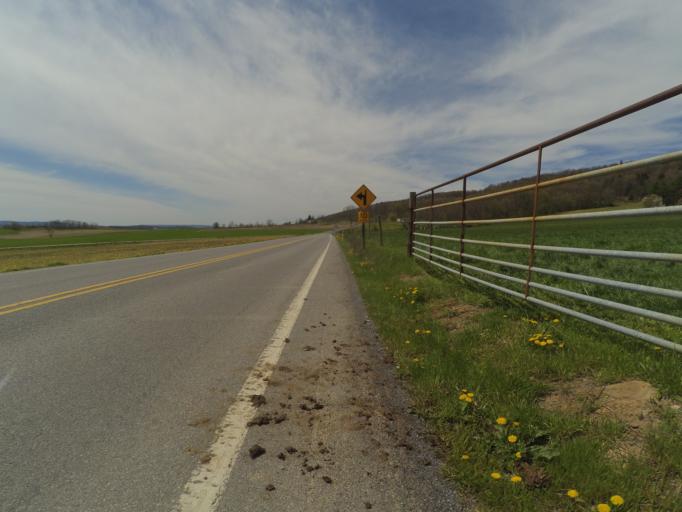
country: US
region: Pennsylvania
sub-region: Centre County
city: Stormstown
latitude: 40.7234
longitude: -78.1165
